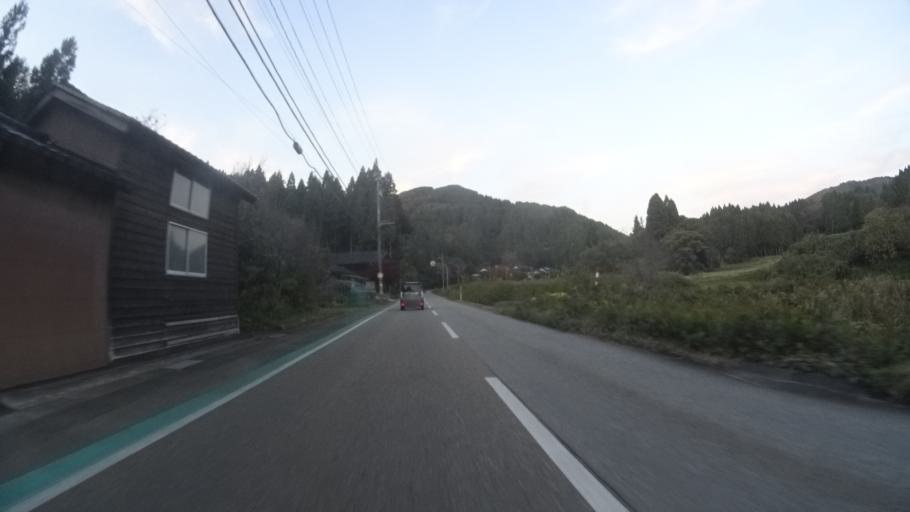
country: JP
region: Ishikawa
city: Nanao
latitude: 37.3107
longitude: 136.7984
